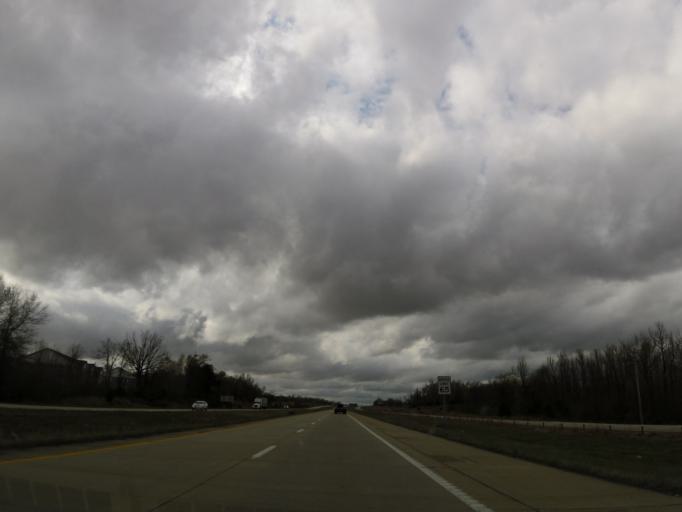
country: US
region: Missouri
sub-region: Butler County
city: Poplar Bluff
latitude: 36.7205
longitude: -90.4656
